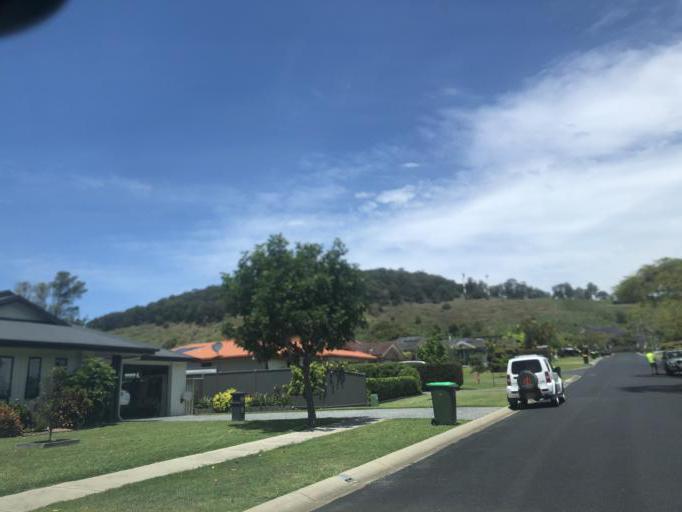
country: AU
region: New South Wales
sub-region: Coffs Harbour
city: Coffs Harbour
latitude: -30.2890
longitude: 153.0925
